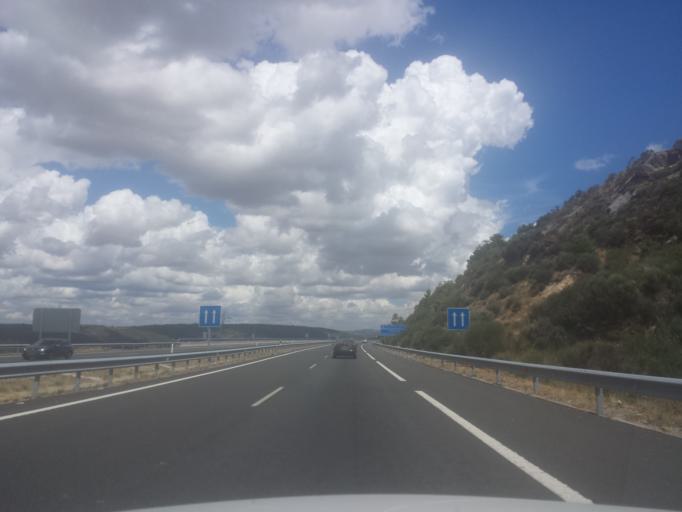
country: ES
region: Castille and Leon
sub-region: Provincia de Salamanca
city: Puerto de Bejar
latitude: 40.3529
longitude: -5.8420
